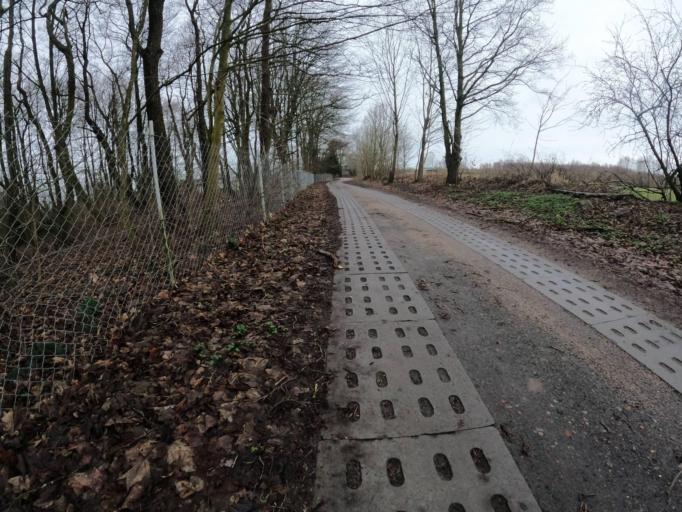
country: PL
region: West Pomeranian Voivodeship
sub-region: Powiat slawienski
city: Darlowo
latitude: 54.4130
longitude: 16.4374
